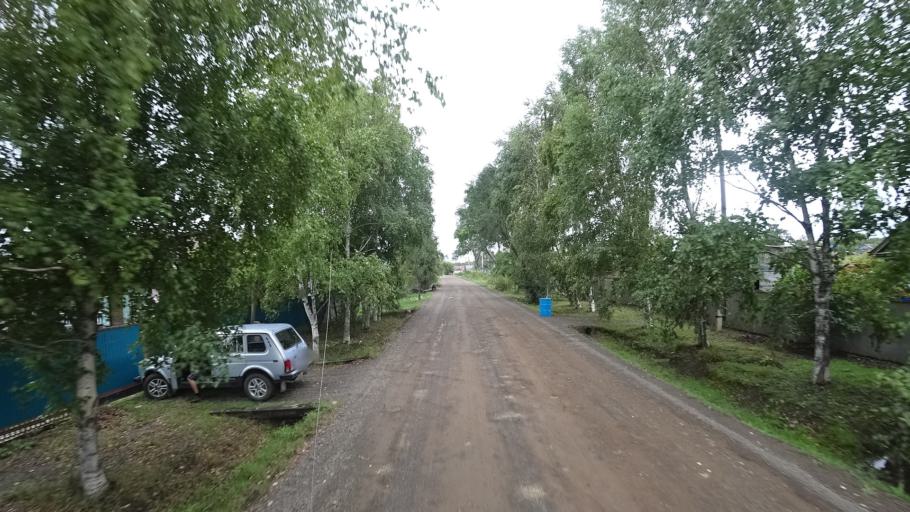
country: RU
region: Primorskiy
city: Chernigovka
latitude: 44.3487
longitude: 132.5724
